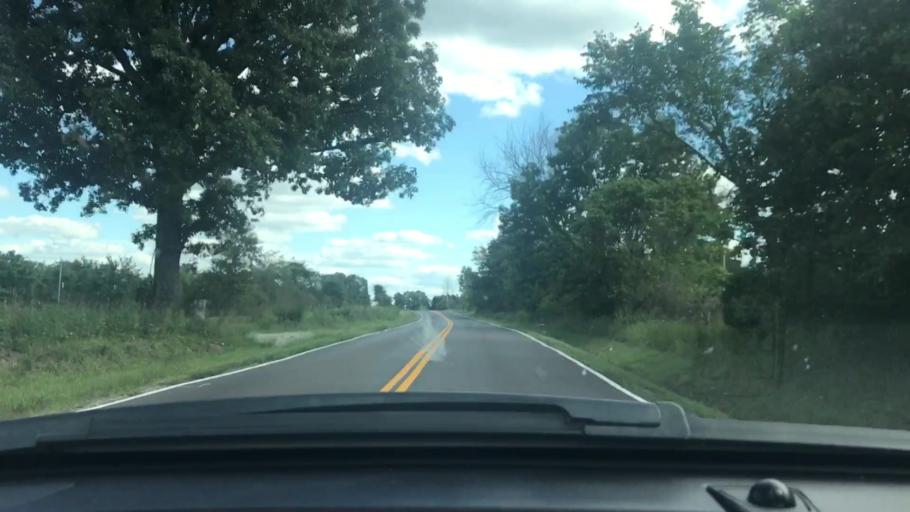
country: US
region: Missouri
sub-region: Wright County
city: Mountain Grove
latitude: 37.3140
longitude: -92.3191
